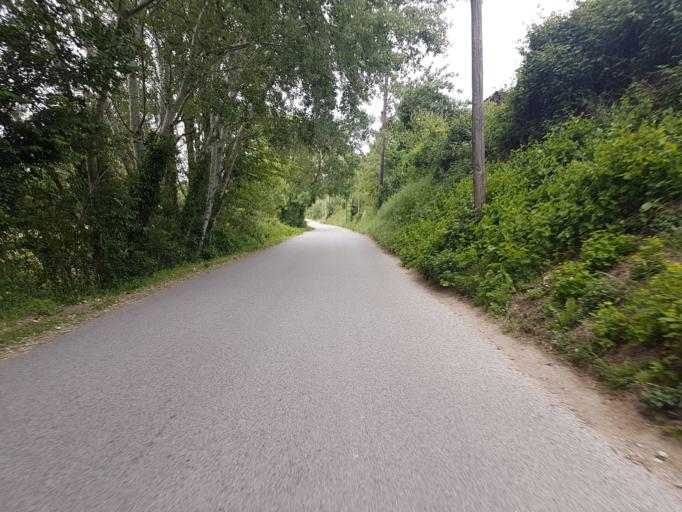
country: FR
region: Languedoc-Roussillon
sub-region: Departement du Gard
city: Sauveterre
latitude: 44.0334
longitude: 4.7881
